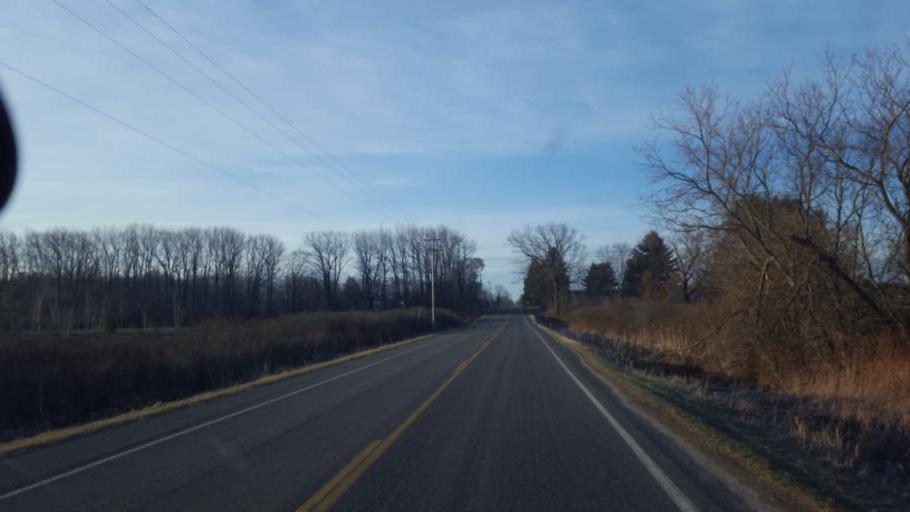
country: US
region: Michigan
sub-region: Montcalm County
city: Edmore
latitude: 43.4319
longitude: -85.0443
